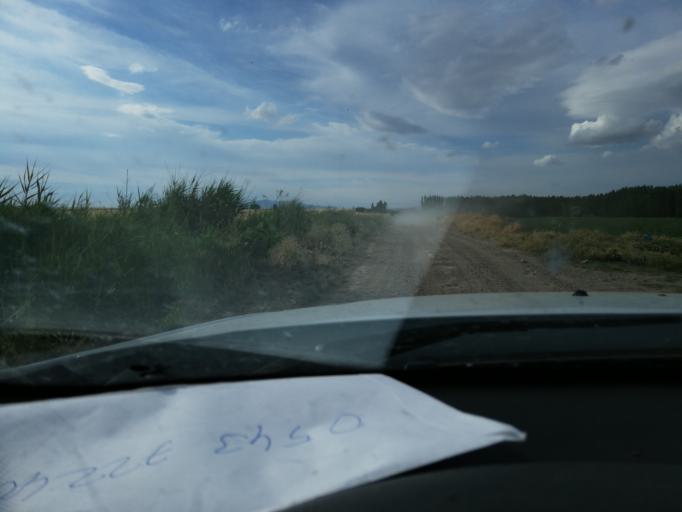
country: TR
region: Kirsehir
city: Kirsehir
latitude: 38.9989
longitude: 34.1247
